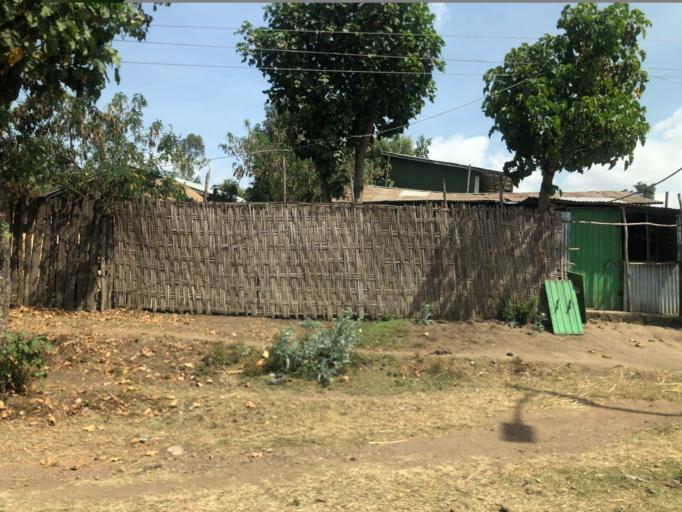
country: ET
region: Oromiya
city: Shashemene
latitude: 7.2741
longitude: 38.6547
